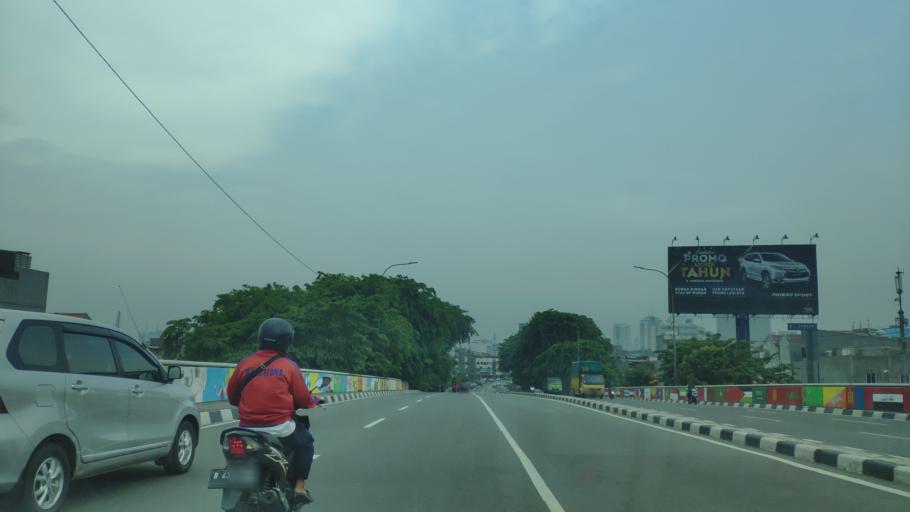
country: ID
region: Jakarta Raya
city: Jakarta
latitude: -6.1732
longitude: 106.8059
